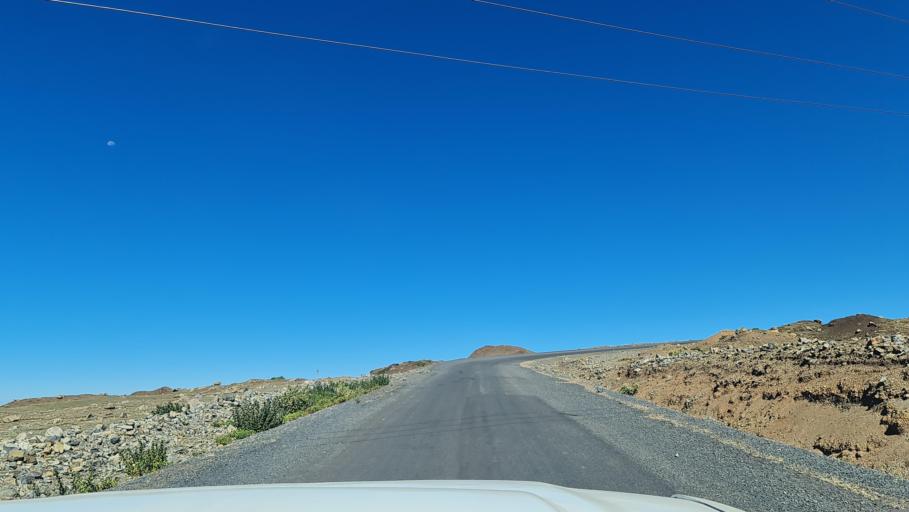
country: ET
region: Amhara
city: Debark'
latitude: 13.1542
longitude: 38.1868
